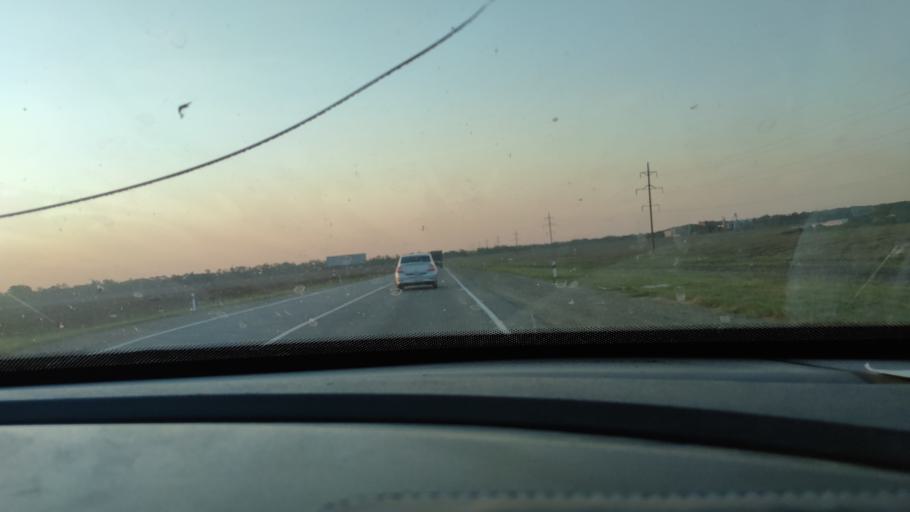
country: RU
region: Krasnodarskiy
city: Starominskaya
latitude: 46.5044
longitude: 39.0369
